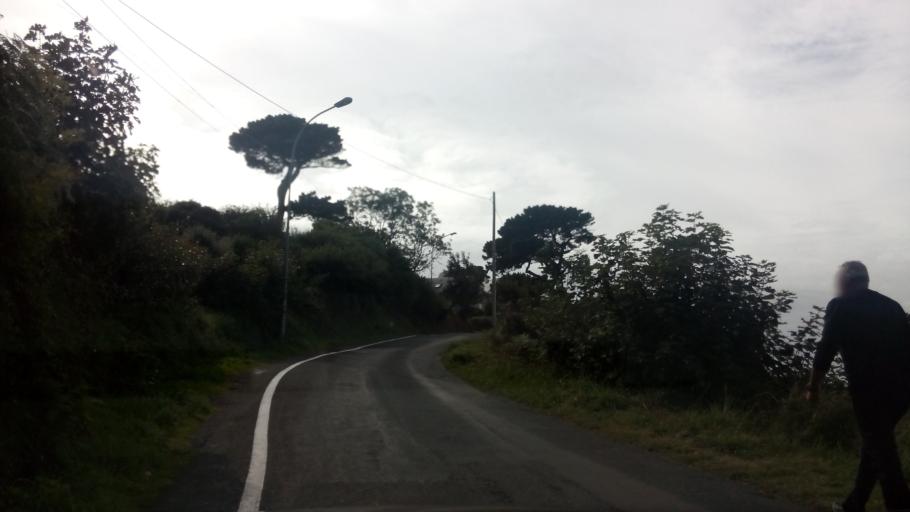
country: FR
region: Brittany
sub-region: Departement des Cotes-d'Armor
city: Perros-Guirec
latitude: 48.8194
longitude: -3.4382
